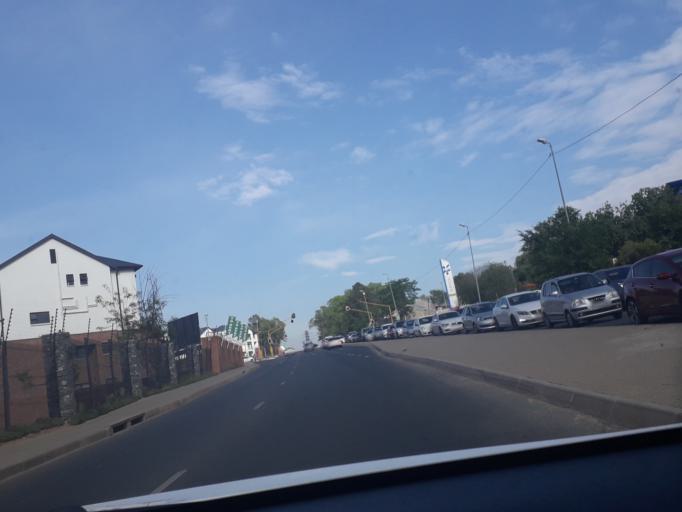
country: ZA
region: Gauteng
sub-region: City of Johannesburg Metropolitan Municipality
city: Diepsloot
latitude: -26.0593
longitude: 27.9793
